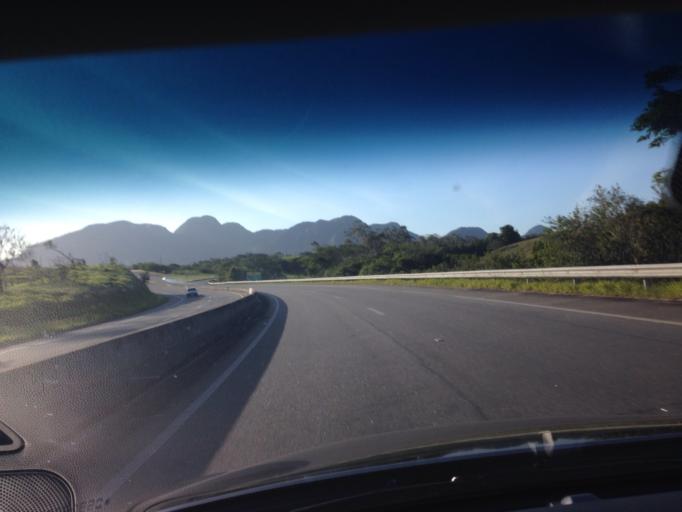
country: BR
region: Espirito Santo
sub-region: Guarapari
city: Guarapari
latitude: -20.6119
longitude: -40.4576
